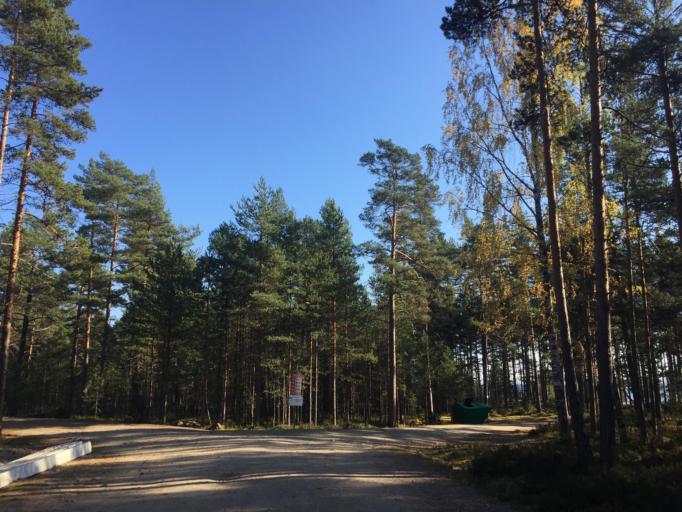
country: RU
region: Leningrad
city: Priozersk
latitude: 61.2803
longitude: 30.0987
